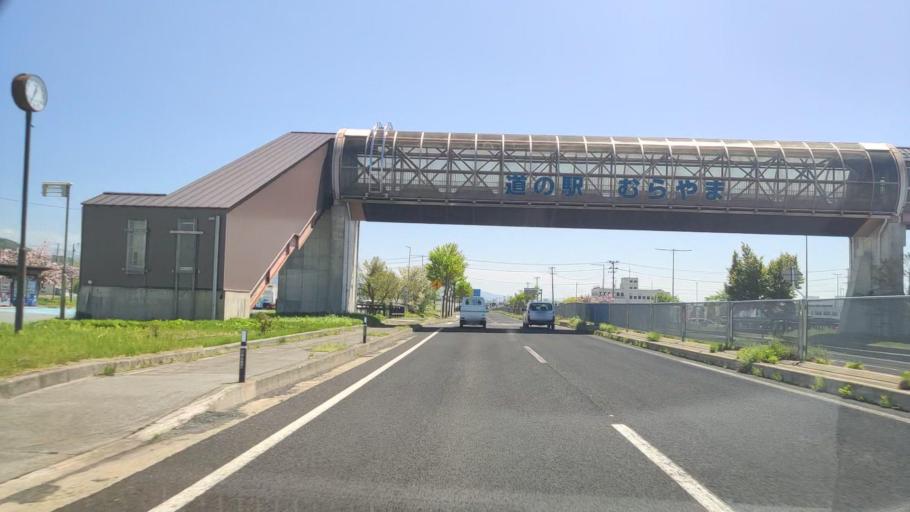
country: JP
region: Yamagata
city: Higashine
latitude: 38.4873
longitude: 140.3831
